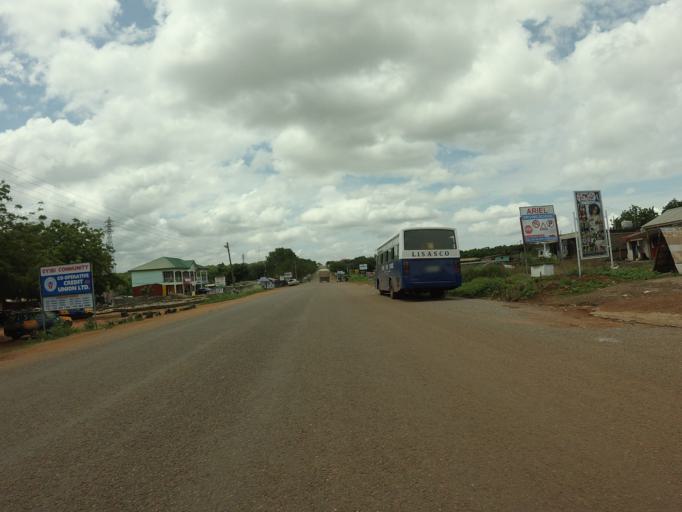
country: GH
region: Eastern
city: Aburi
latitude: 5.8053
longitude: -0.1251
